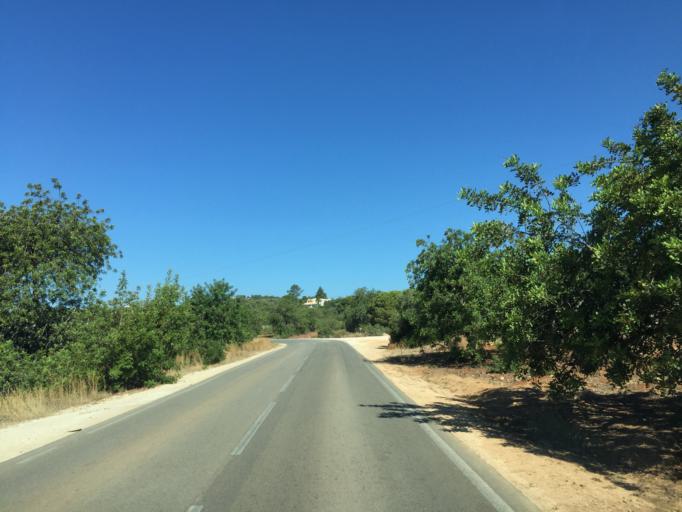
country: PT
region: Faro
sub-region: Loule
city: Vilamoura
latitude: 37.1153
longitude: -8.0766
